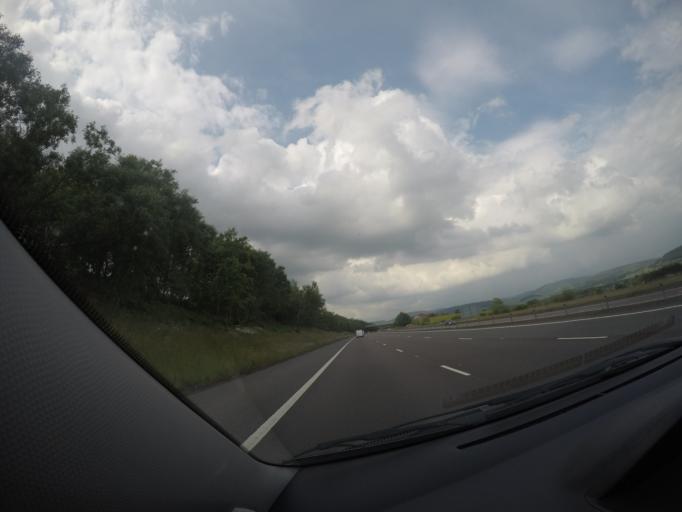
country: GB
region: Scotland
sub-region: Dumfries and Galloway
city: Lochmaben
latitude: 55.2321
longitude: -3.4128
